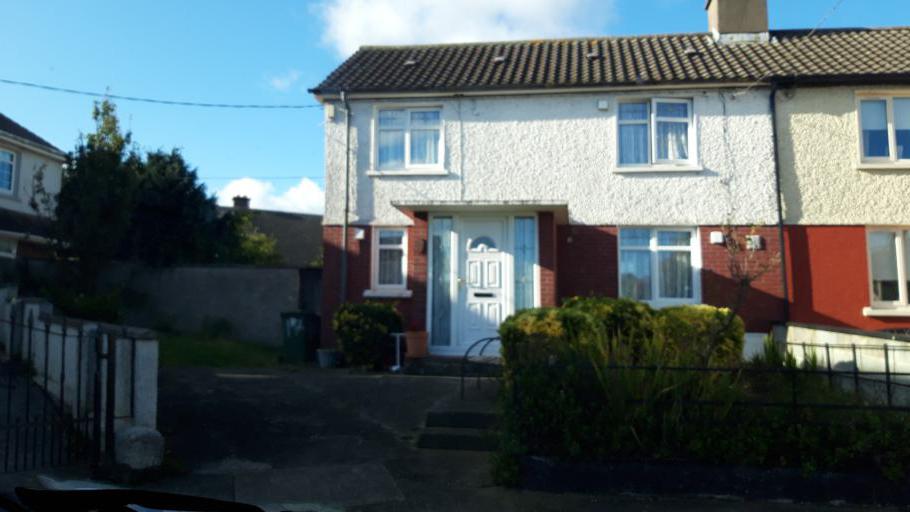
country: IE
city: Coolock
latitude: 53.3870
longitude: -6.1949
